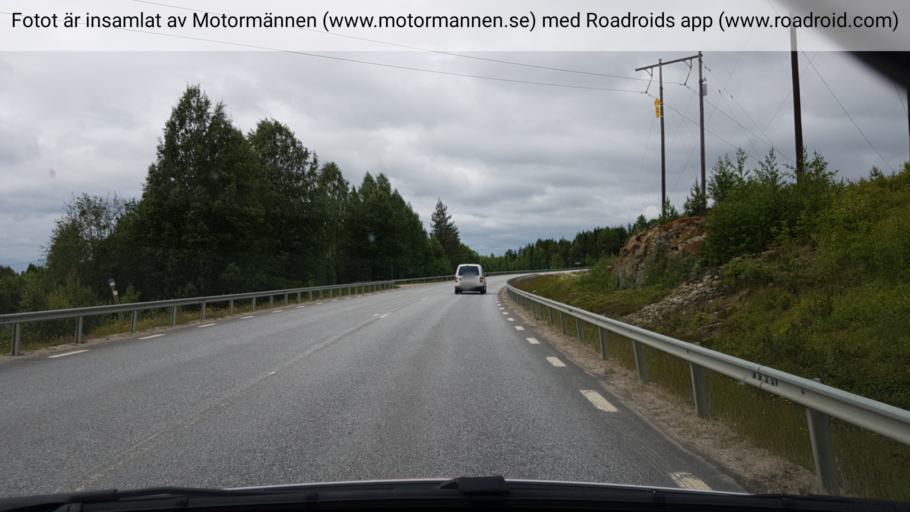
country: SE
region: Vaesterbotten
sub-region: Vannas Kommun
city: Vaennaes
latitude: 63.9686
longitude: 19.7427
